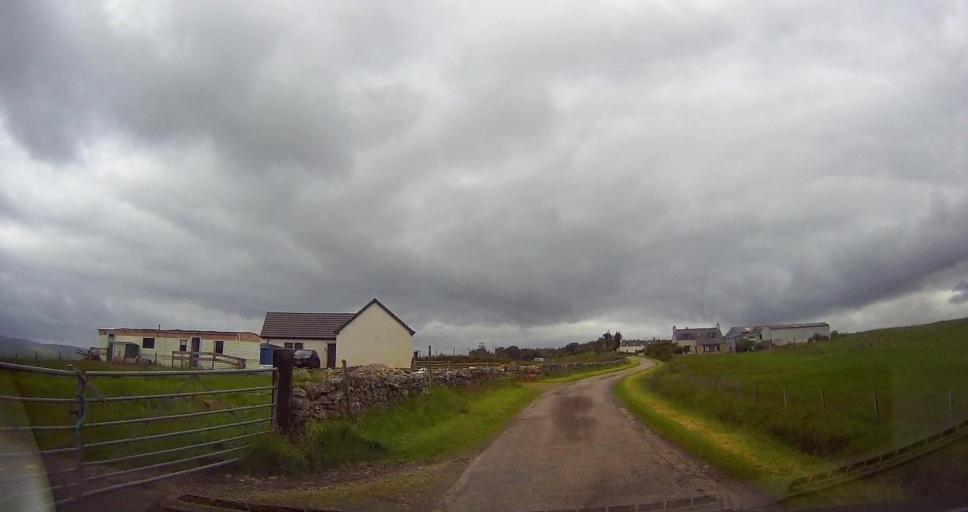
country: GB
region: Scotland
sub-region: Highland
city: Alness
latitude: 58.0769
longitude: -4.4436
